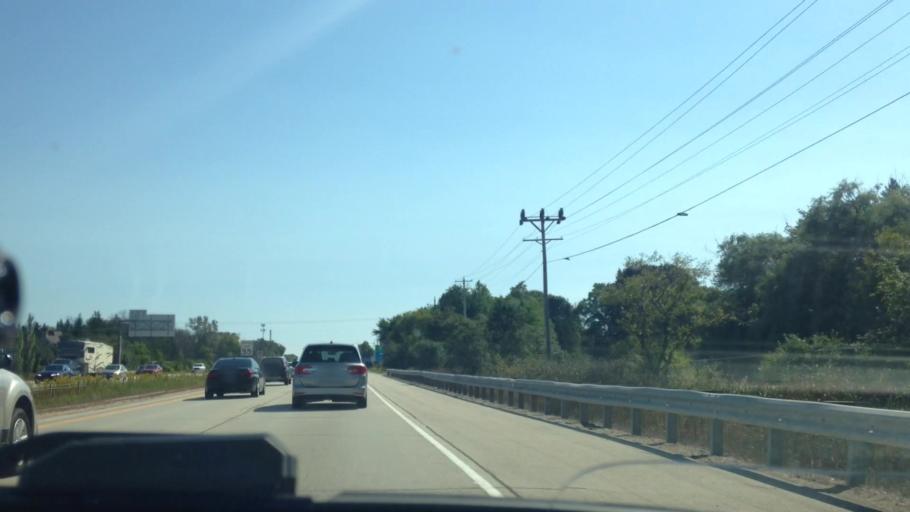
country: US
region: Wisconsin
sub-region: Milwaukee County
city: River Hills
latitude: 43.1855
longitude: -87.9219
